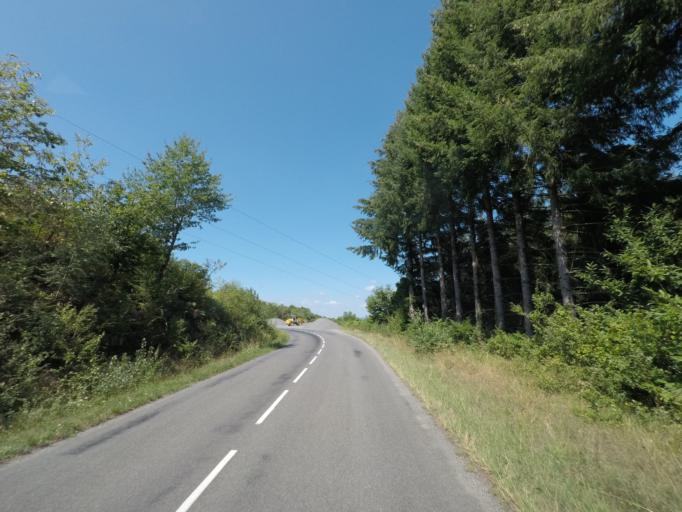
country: FR
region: Midi-Pyrenees
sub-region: Departement de l'Aveyron
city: Livinhac-le-Haut
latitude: 44.6176
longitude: 2.2072
